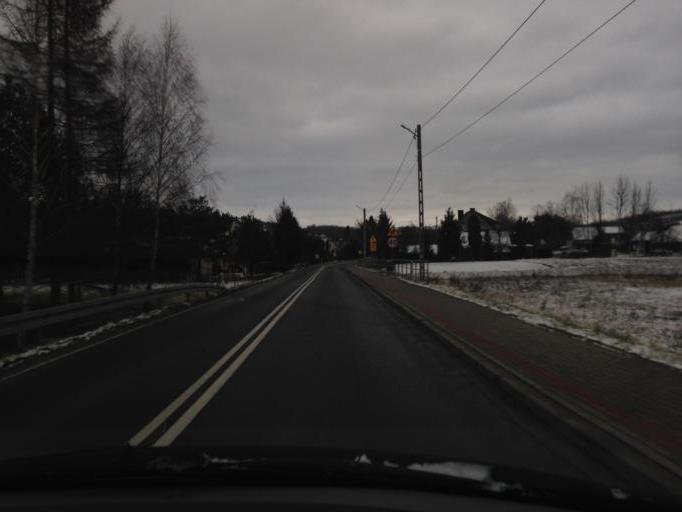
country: PL
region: Lesser Poland Voivodeship
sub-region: Powiat tarnowski
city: Gromnik
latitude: 49.8396
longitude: 20.9820
